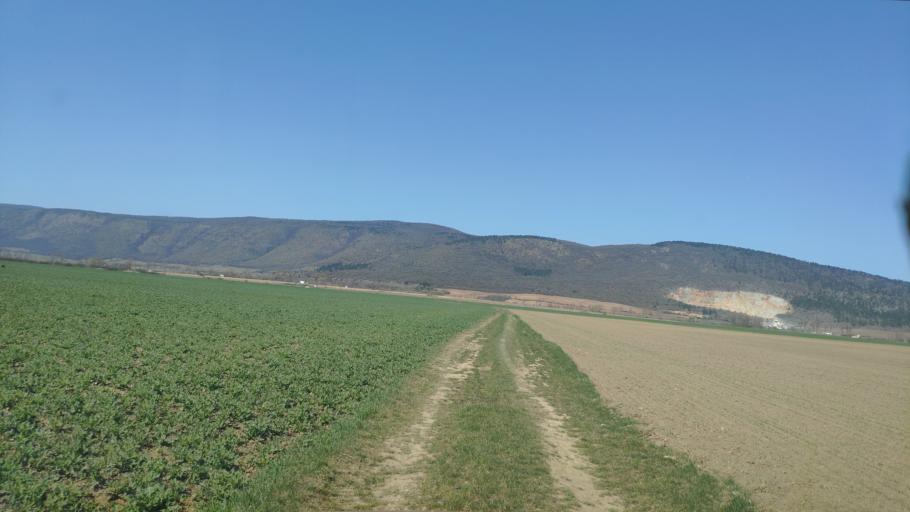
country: SK
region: Kosicky
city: Moldava nad Bodvou
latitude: 48.5989
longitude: 20.9321
